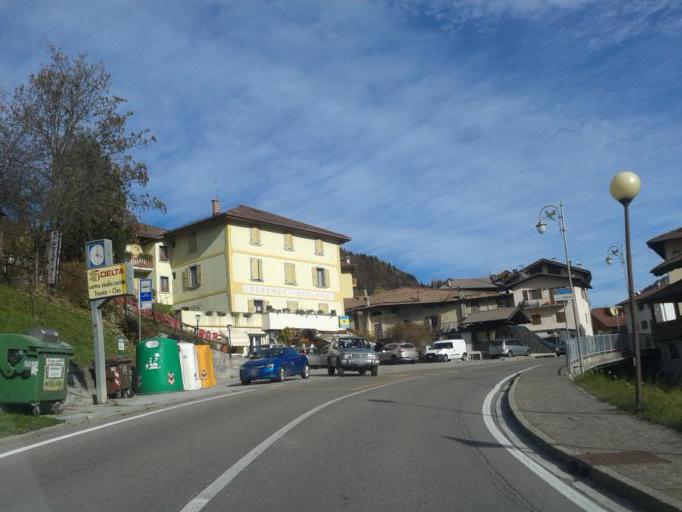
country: IT
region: Trentino-Alto Adige
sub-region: Provincia di Trento
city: Roncone
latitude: 45.9833
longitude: 10.6705
